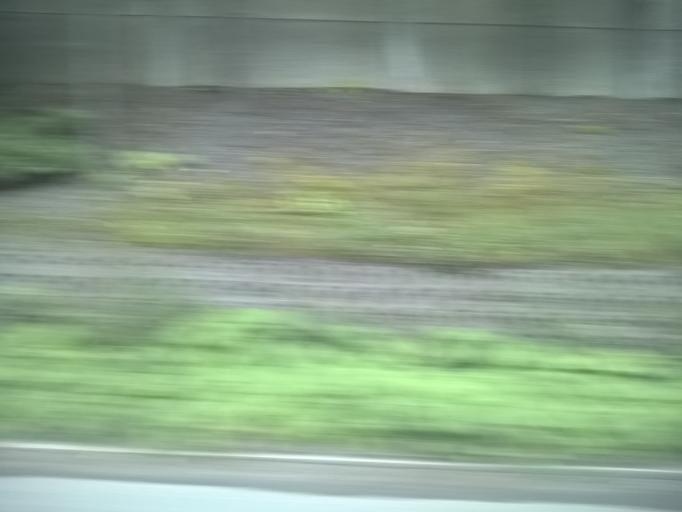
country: FI
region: Pirkanmaa
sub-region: Tampere
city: Tampere
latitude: 61.5060
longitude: 23.7918
